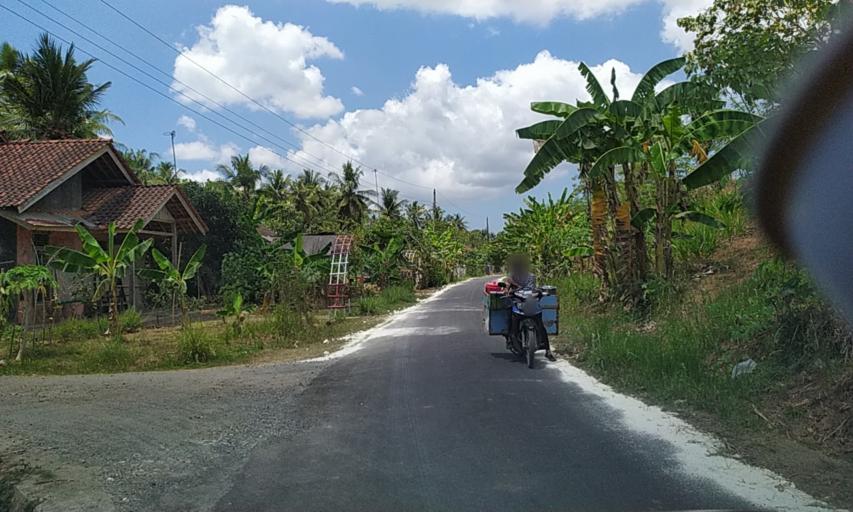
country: ID
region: Central Java
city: Kedungsalam
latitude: -7.6194
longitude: 108.7472
